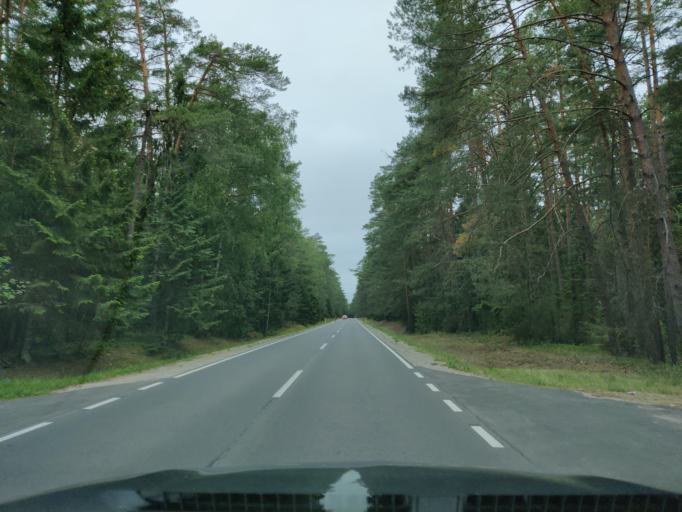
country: PL
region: Masovian Voivodeship
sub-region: Powiat ostrolecki
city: Czarnia
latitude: 53.3351
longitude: 21.2169
